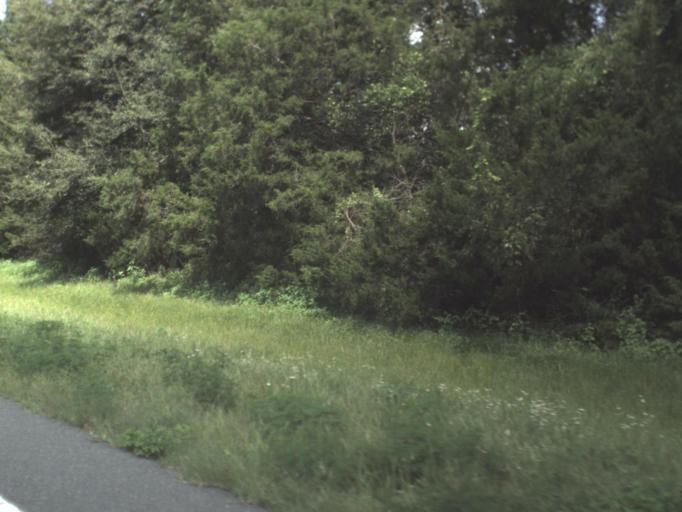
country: US
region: Florida
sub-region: Alachua County
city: Alachua
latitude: 29.8216
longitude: -82.4399
